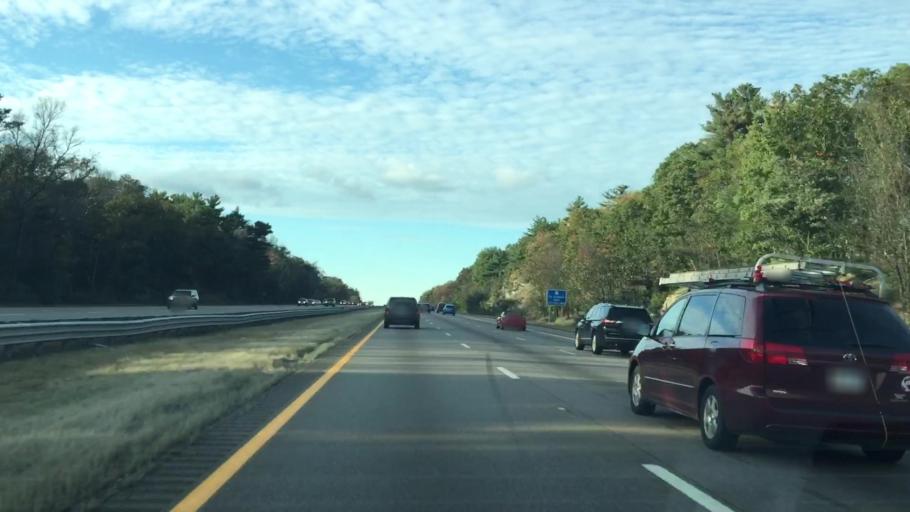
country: US
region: Massachusetts
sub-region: Norfolk County
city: Randolph
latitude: 42.1685
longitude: -71.0721
